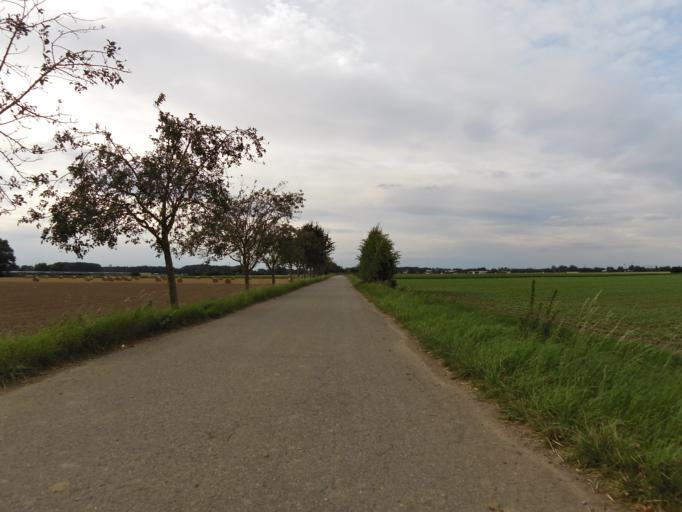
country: DE
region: Rheinland-Pfalz
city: Worms
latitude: 49.6220
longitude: 8.4070
